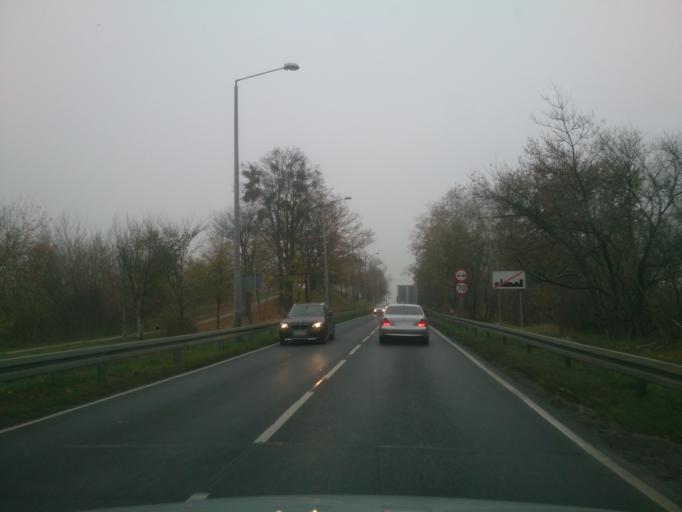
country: PL
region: Kujawsko-Pomorskie
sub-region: Powiat brodnicki
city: Brodnica
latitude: 53.2607
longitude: 19.3779
